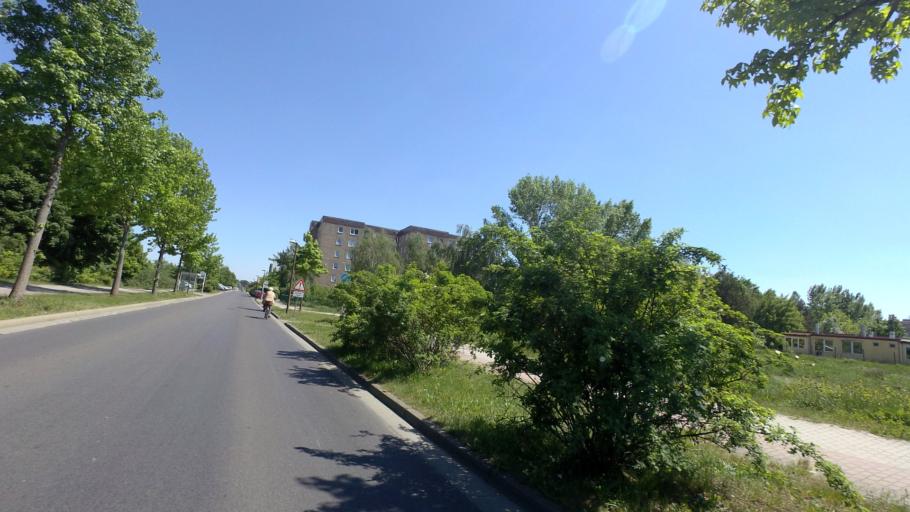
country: DE
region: Brandenburg
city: Cottbus
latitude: 51.7857
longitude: 14.3379
